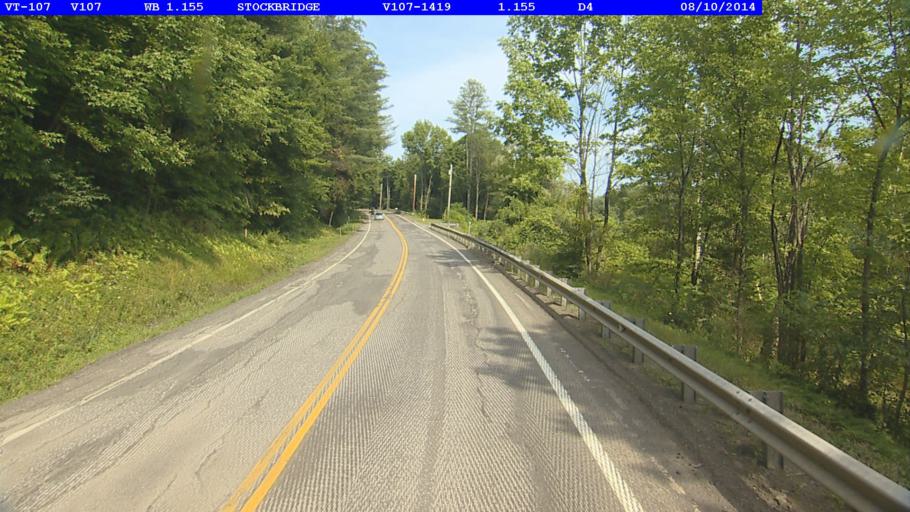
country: US
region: Vermont
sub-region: Orange County
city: Randolph
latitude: 43.7659
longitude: -72.7442
